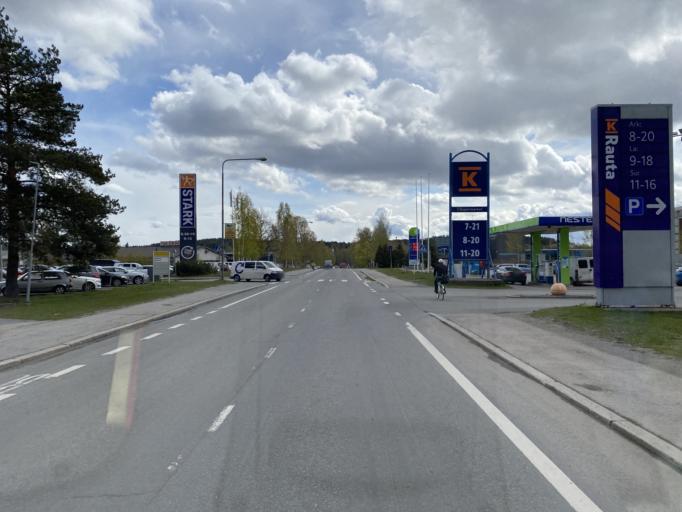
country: FI
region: Pirkanmaa
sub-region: Tampere
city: Tampere
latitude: 61.4801
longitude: 23.7827
